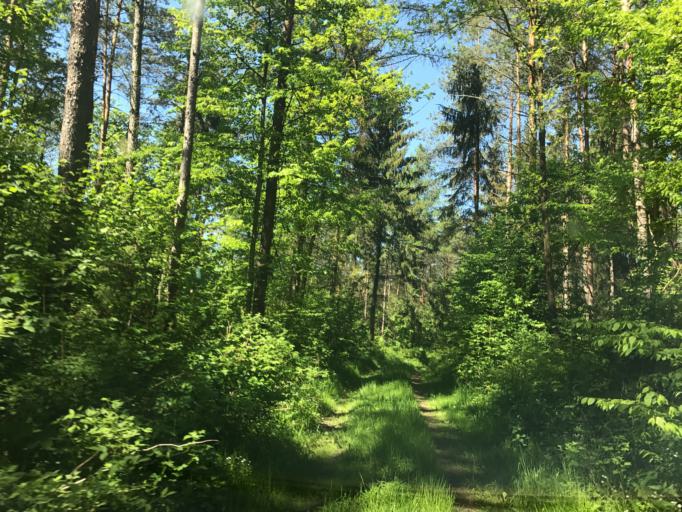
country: PL
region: Warmian-Masurian Voivodeship
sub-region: Powiat dzialdowski
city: Lidzbark
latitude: 53.2442
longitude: 19.7555
